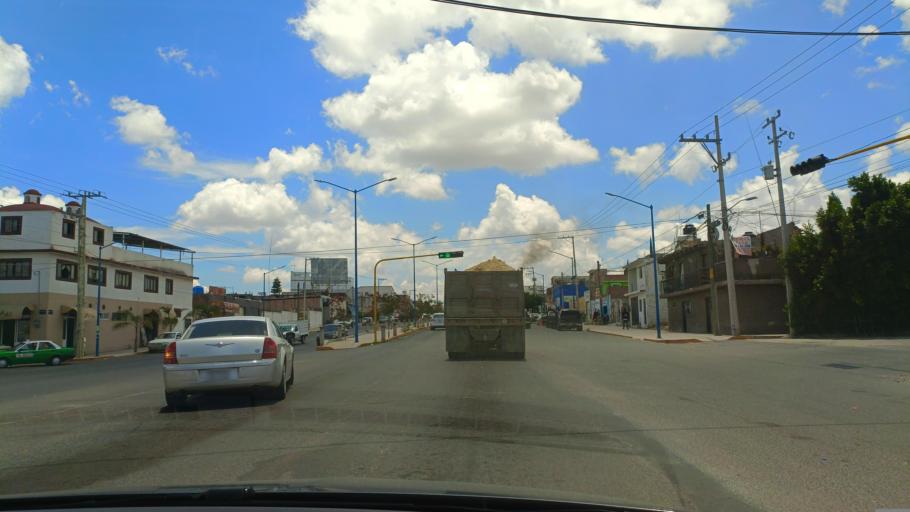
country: MX
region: Guerrero
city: San Luis de la Paz
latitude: 21.2883
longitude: -100.5150
